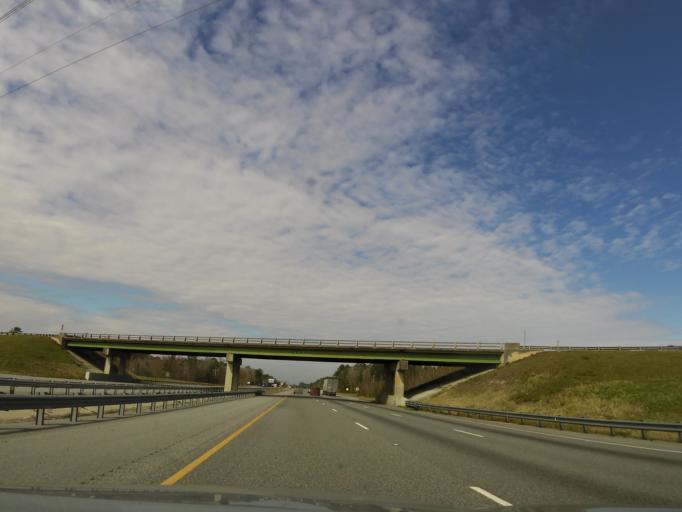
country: US
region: Georgia
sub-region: McIntosh County
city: Darien
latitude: 31.5312
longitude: -81.4450
